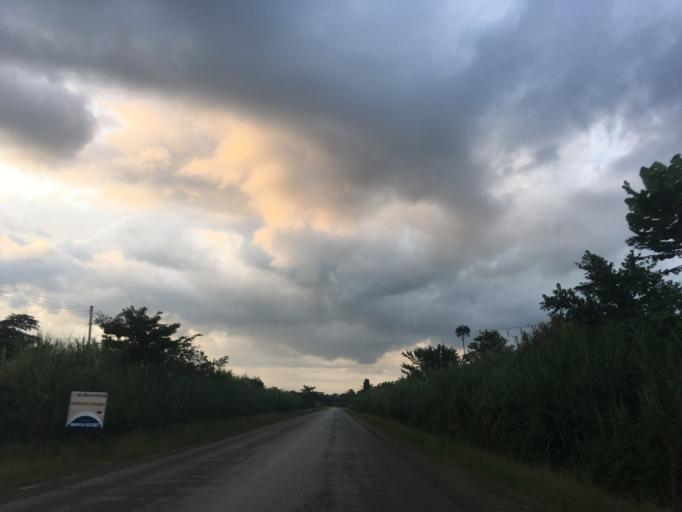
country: GH
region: Western
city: Bibiani
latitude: 6.7553
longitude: -2.5043
